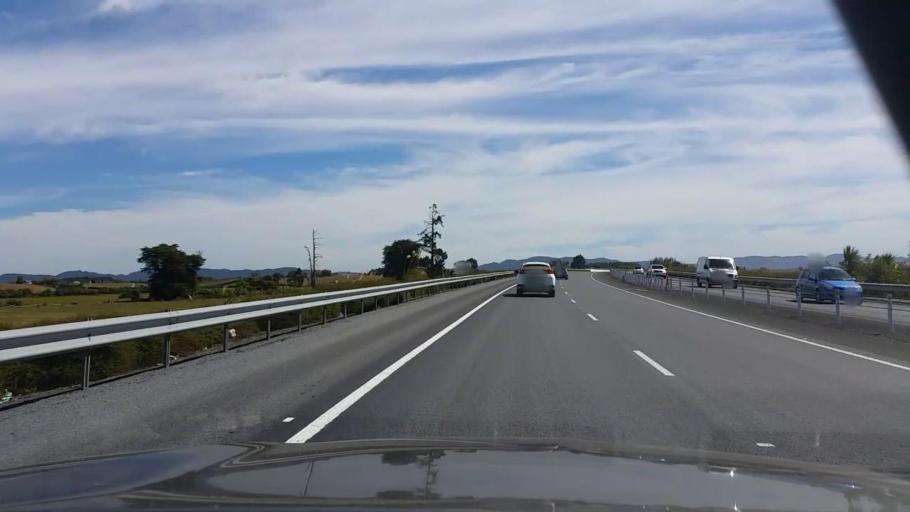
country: NZ
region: Waikato
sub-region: Hamilton City
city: Hamilton
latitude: -37.7505
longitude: 175.2180
